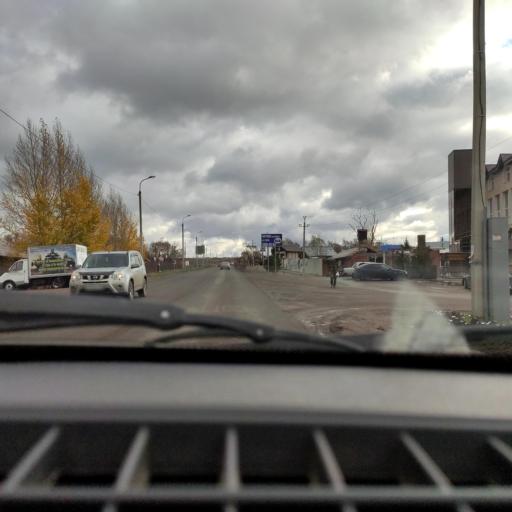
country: RU
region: Bashkortostan
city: Kabakovo
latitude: 54.6415
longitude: 56.0860
